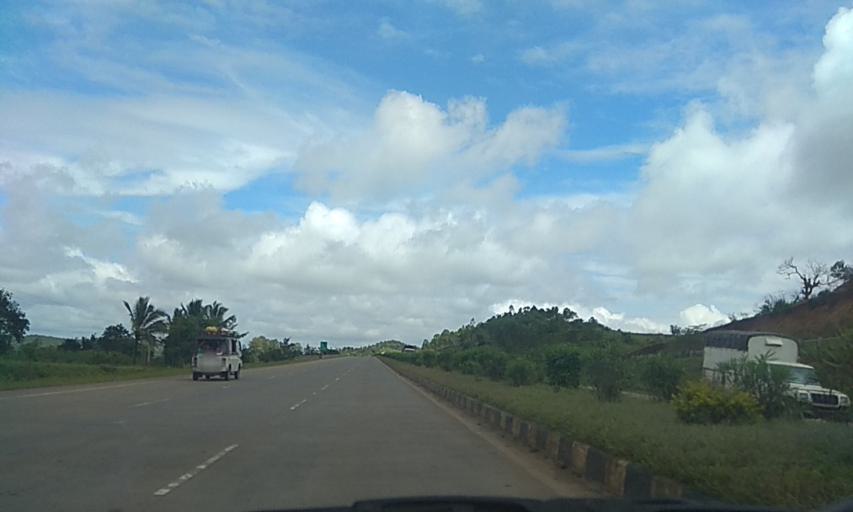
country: IN
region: Karnataka
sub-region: Dharwad
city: Alnavar
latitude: 15.6081
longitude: 74.7688
